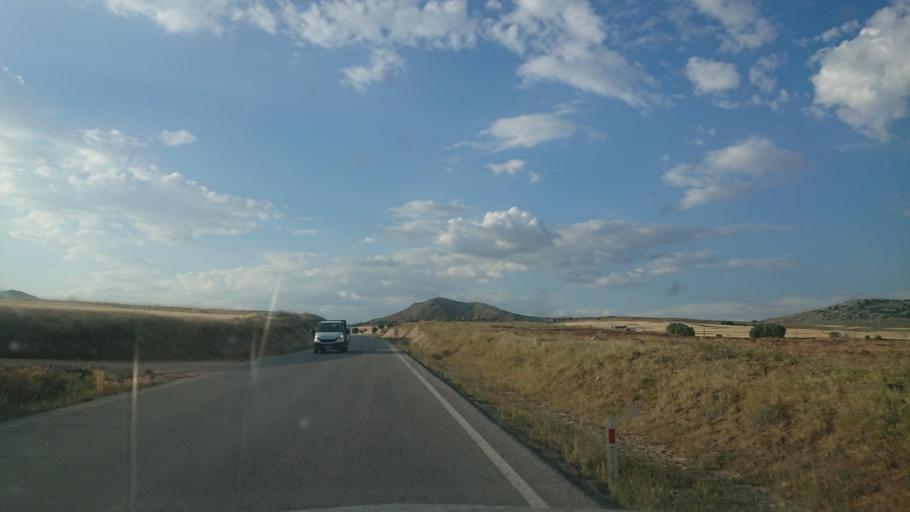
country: TR
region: Aksaray
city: Balci
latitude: 38.5761
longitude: 34.1053
